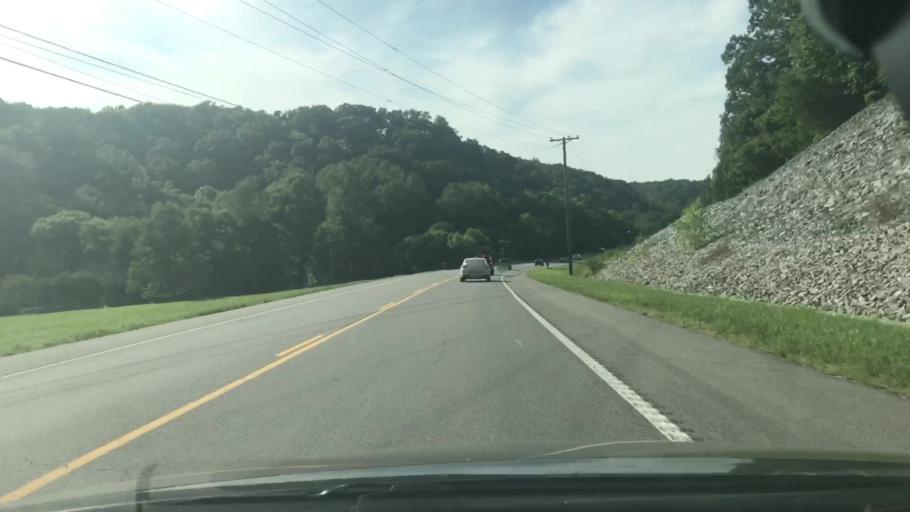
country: US
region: Tennessee
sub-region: Williamson County
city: Franklin
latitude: 35.9726
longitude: -86.9803
